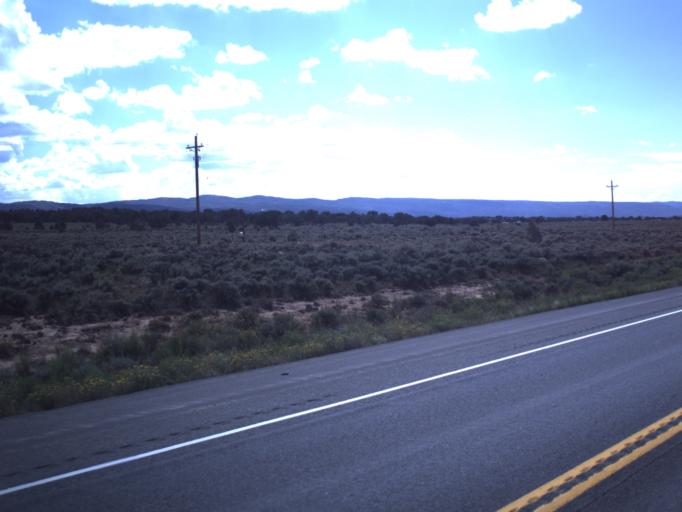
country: US
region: Utah
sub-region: Duchesne County
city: Duchesne
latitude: 40.2039
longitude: -110.7189
